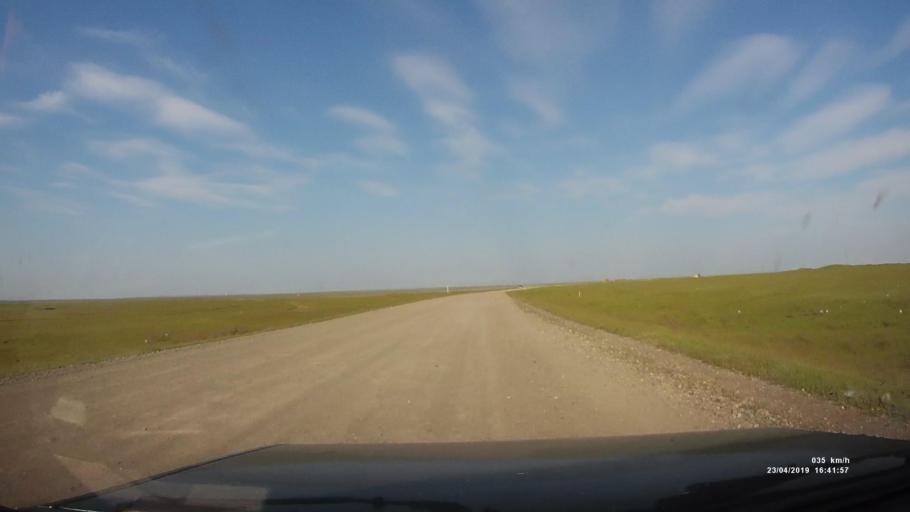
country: RU
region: Kalmykiya
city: Priyutnoye
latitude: 46.3471
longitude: 43.1904
